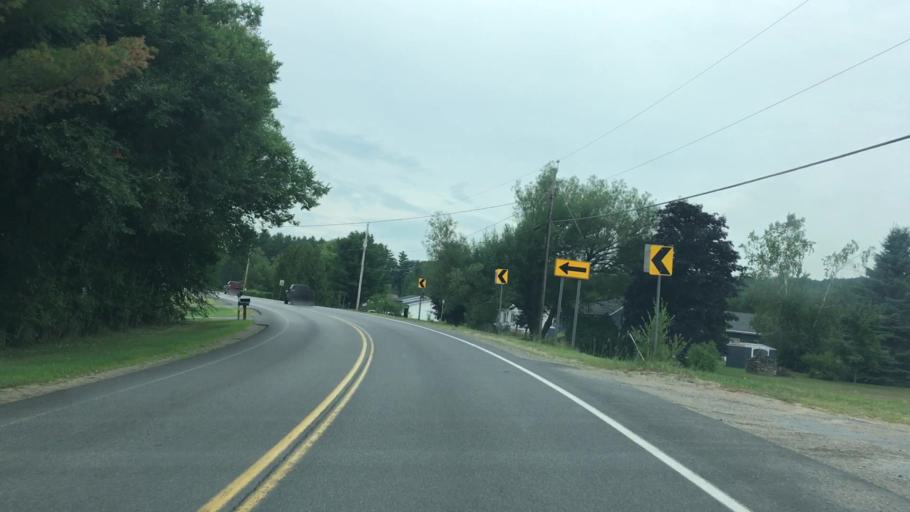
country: US
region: New York
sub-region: Clinton County
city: Peru
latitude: 44.5184
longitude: -73.5805
